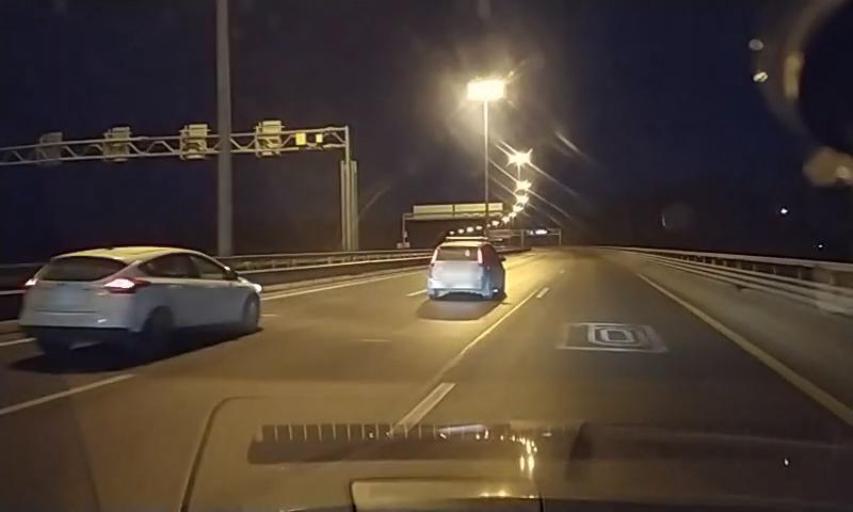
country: RU
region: St.-Petersburg
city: Pesochnyy
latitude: 60.0689
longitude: 30.1376
